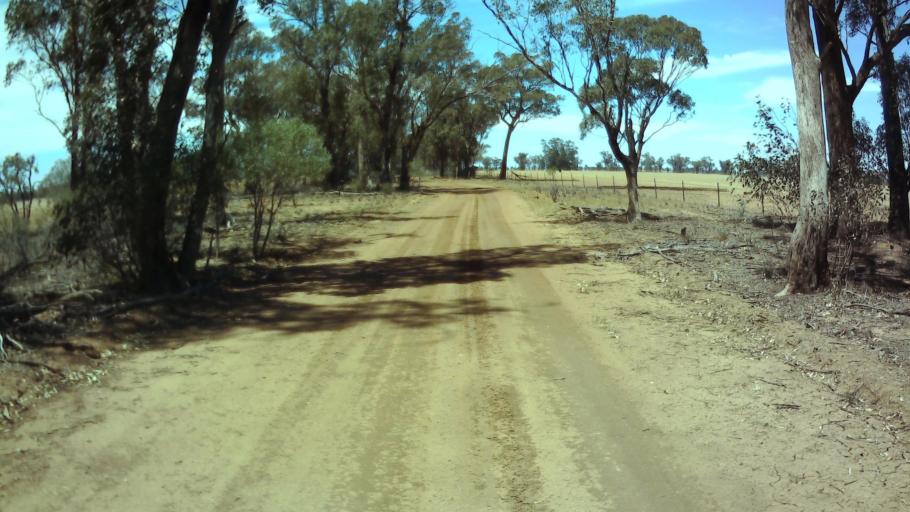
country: AU
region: New South Wales
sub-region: Weddin
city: Grenfell
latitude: -33.9243
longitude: 147.8040
